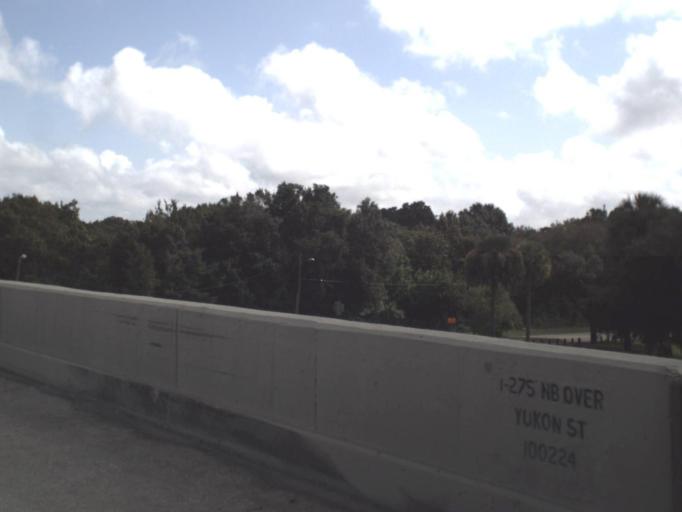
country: US
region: Florida
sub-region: Hillsborough County
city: Carrollwood
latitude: 28.0287
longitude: -82.4550
